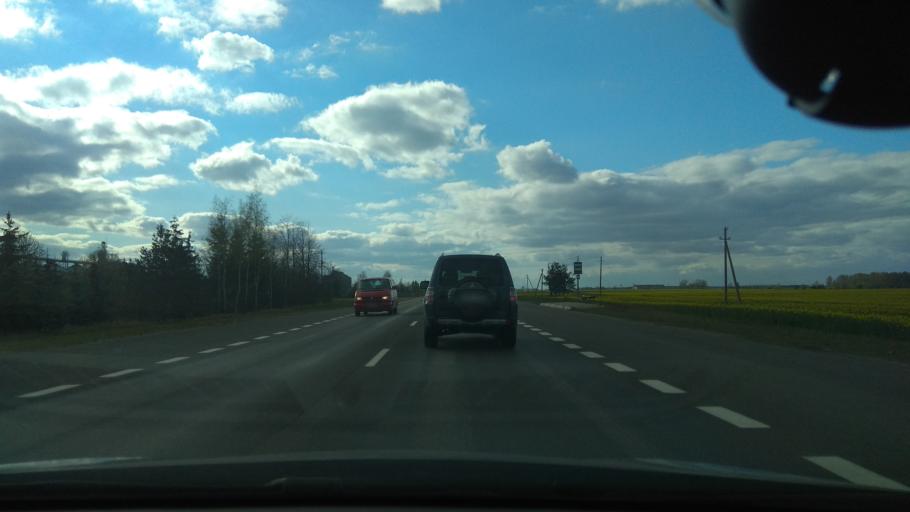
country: LT
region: Panevezys
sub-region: Panevezys City
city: Panevezys
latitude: 55.7463
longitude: 24.1620
